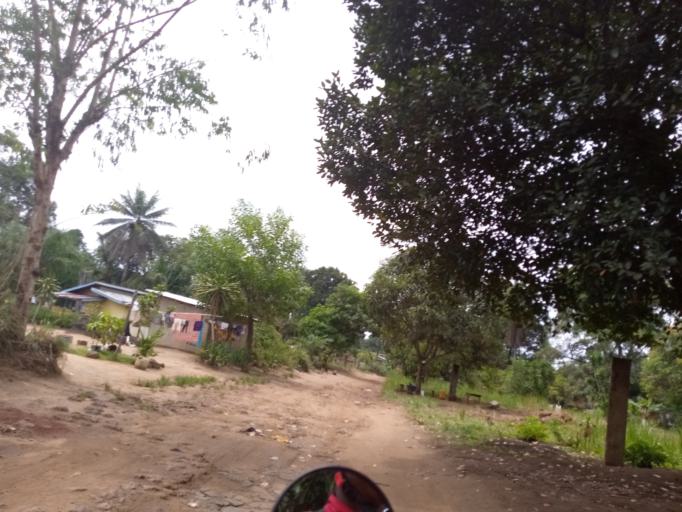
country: SL
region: Western Area
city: Waterloo
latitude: 8.3333
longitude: -13.0115
